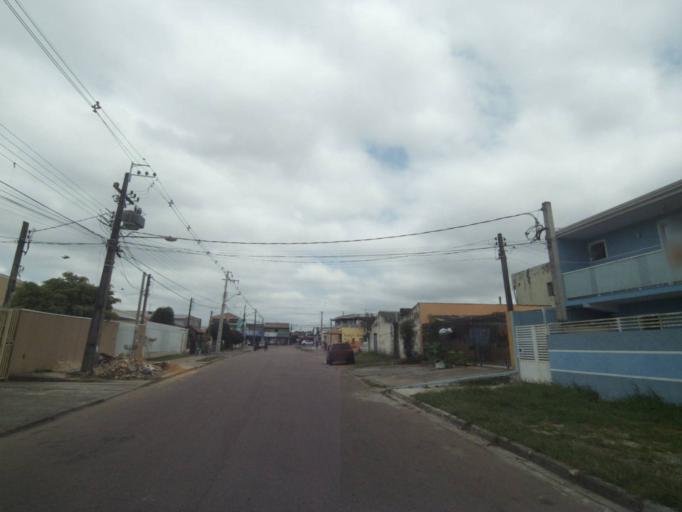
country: BR
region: Parana
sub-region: Sao Jose Dos Pinhais
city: Sao Jose dos Pinhais
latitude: -25.5373
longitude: -49.2682
